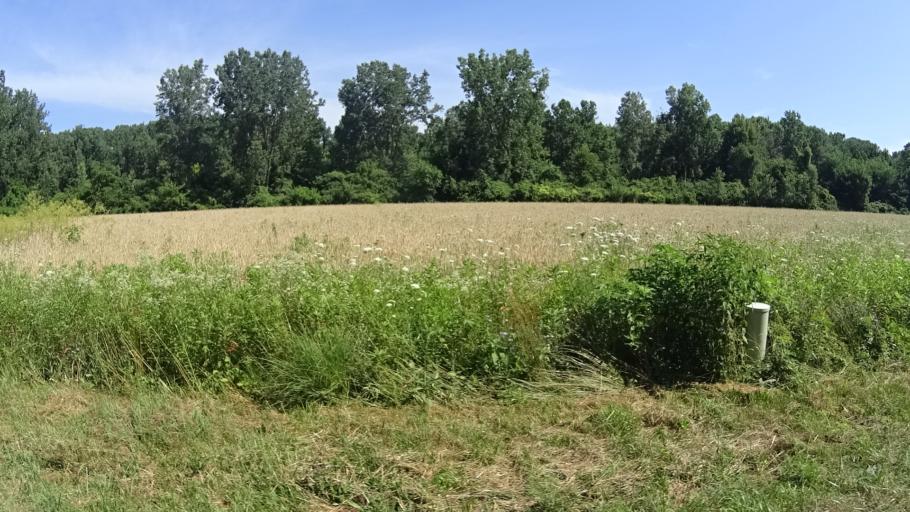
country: US
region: Ohio
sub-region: Huron County
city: Bellevue
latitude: 41.4084
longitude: -82.8417
